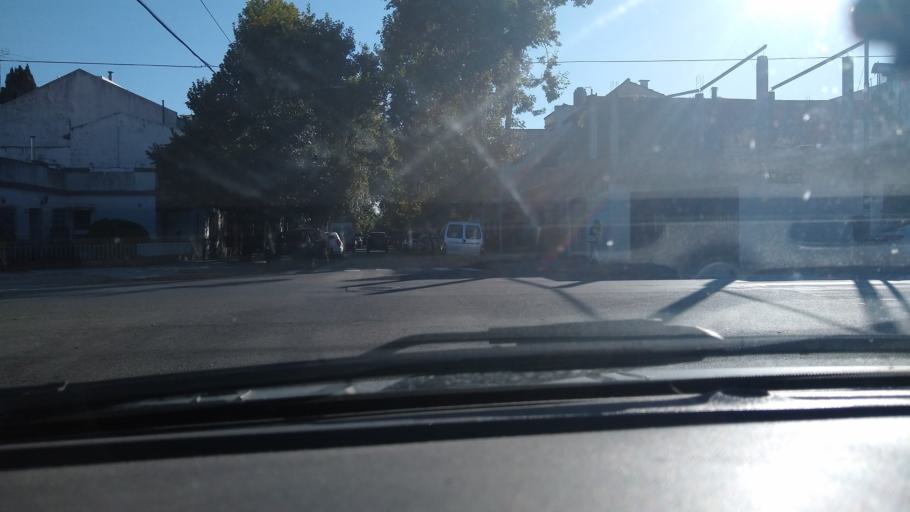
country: AR
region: Buenos Aires F.D.
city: Villa Santa Rita
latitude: -34.6084
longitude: -58.5136
